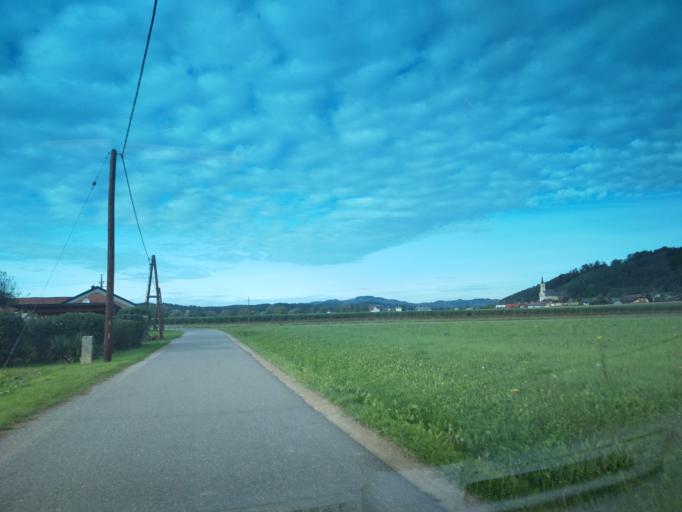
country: AT
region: Styria
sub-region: Politischer Bezirk Leibnitz
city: Sankt Johann im Saggautal
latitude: 46.6943
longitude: 15.3928
